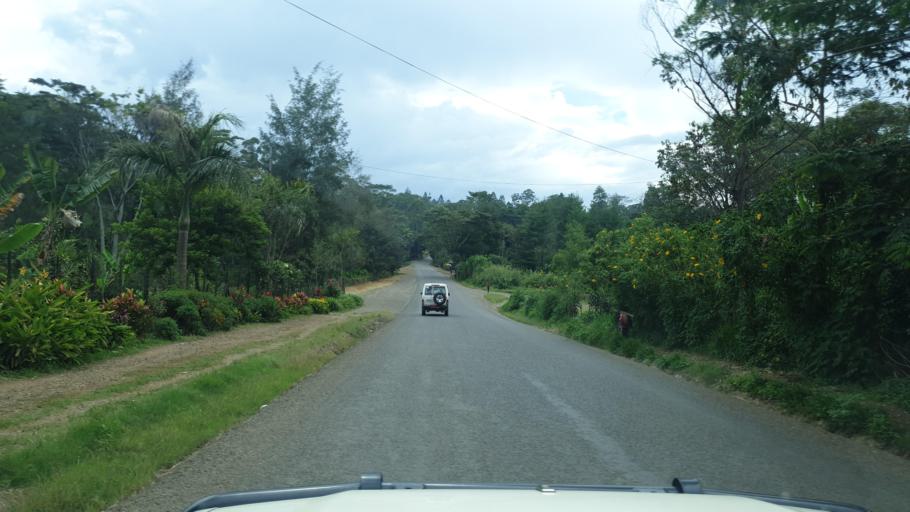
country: PG
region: Eastern Highlands
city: Goroka
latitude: -6.0460
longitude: 145.3771
